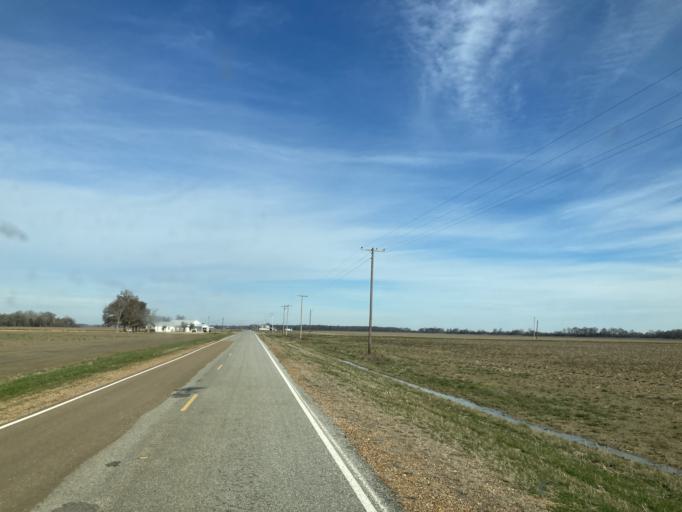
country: US
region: Mississippi
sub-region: Humphreys County
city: Belzoni
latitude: 33.0212
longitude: -90.6230
